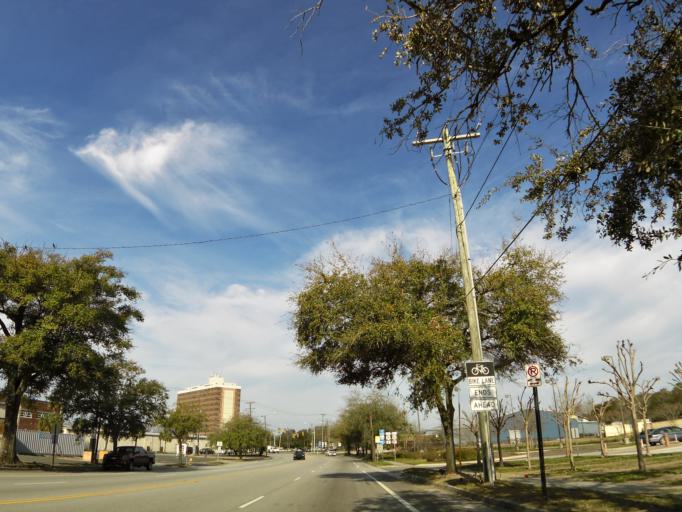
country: US
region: South Carolina
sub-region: Charleston County
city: Charleston
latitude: 32.8115
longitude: -79.9489
